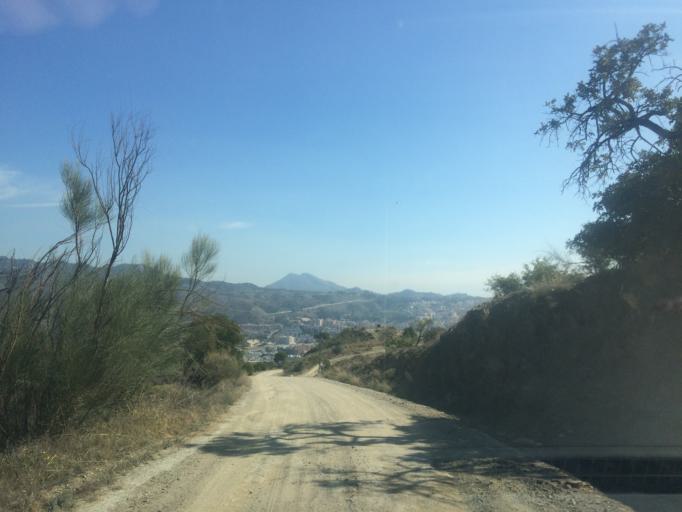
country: ES
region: Andalusia
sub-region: Provincia de Malaga
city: Malaga
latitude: 36.7539
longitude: -4.4413
